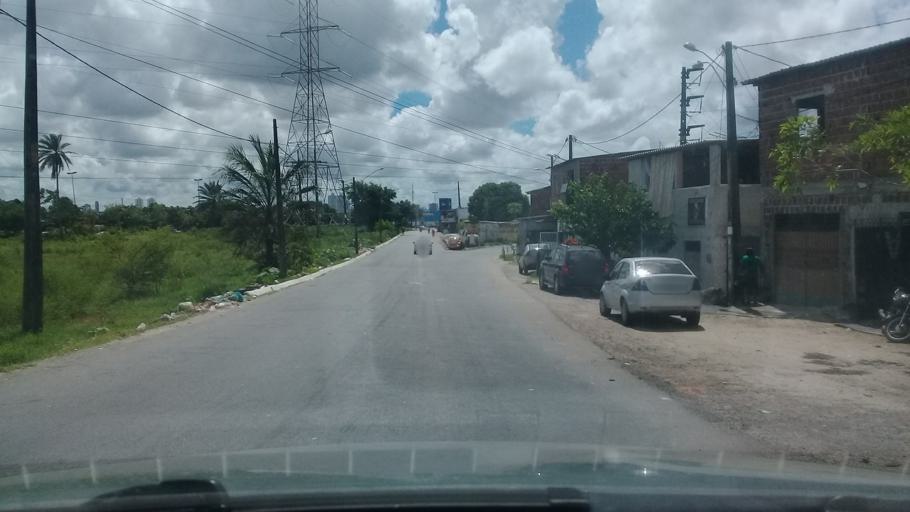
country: BR
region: Pernambuco
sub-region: Recife
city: Recife
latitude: -8.0675
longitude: -34.9400
